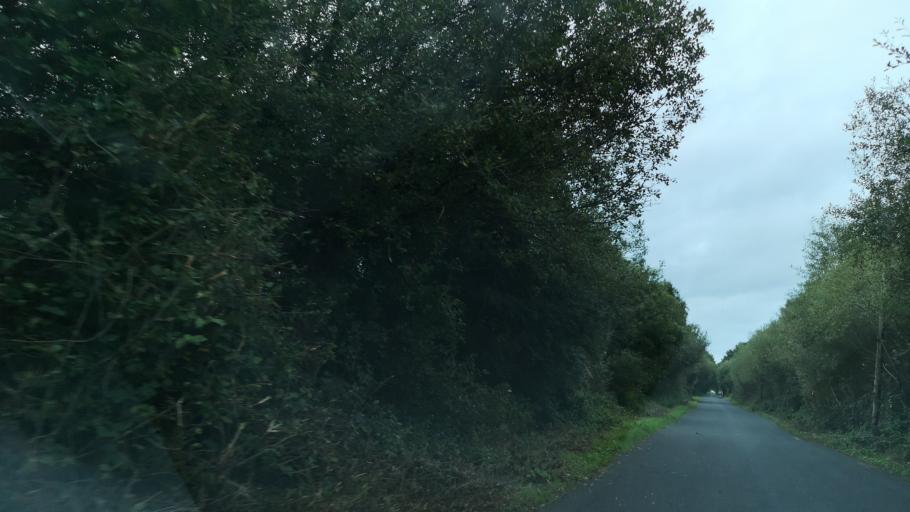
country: IE
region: Leinster
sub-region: Uibh Fhaili
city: Ferbane
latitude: 53.1953
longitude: -7.7784
